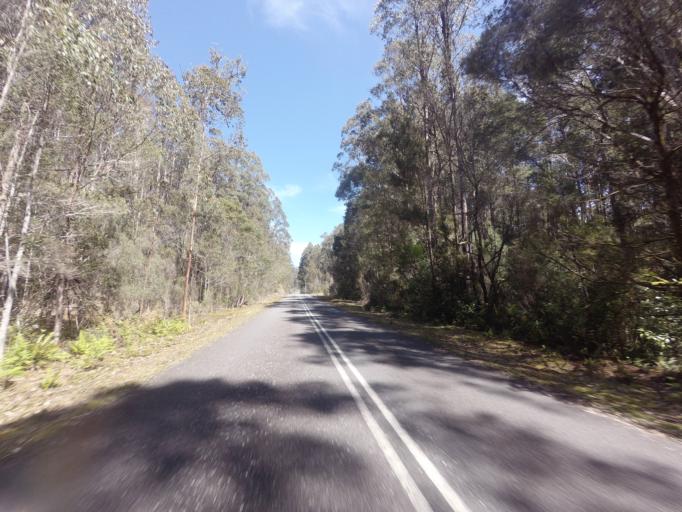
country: AU
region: Tasmania
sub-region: Huon Valley
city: Geeveston
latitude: -42.8365
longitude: 146.2653
